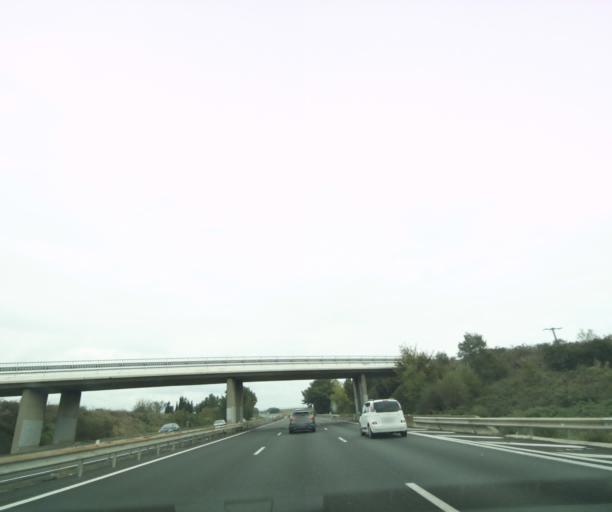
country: FR
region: Languedoc-Roussillon
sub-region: Departement de l'Herault
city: Pinet
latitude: 43.4094
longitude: 3.5032
